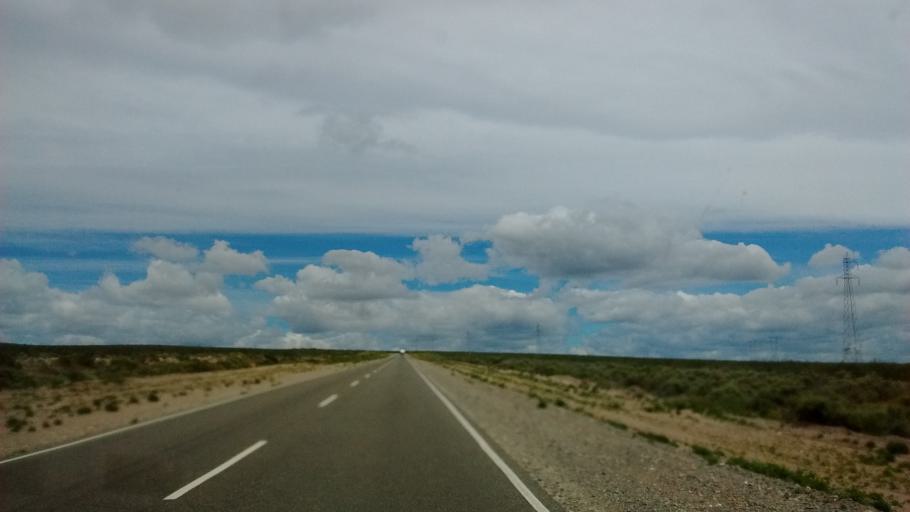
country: AR
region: Neuquen
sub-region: Departamento de Picun Leufu
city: Picun Leufu
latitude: -39.7302
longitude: -69.5746
